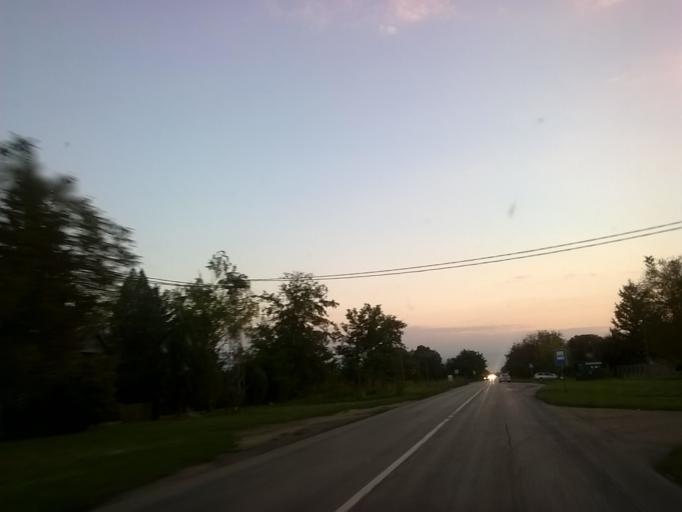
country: RS
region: Autonomna Pokrajina Vojvodina
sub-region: Juznobanatski Okrug
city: Pancevo
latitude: 44.9258
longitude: 20.6619
